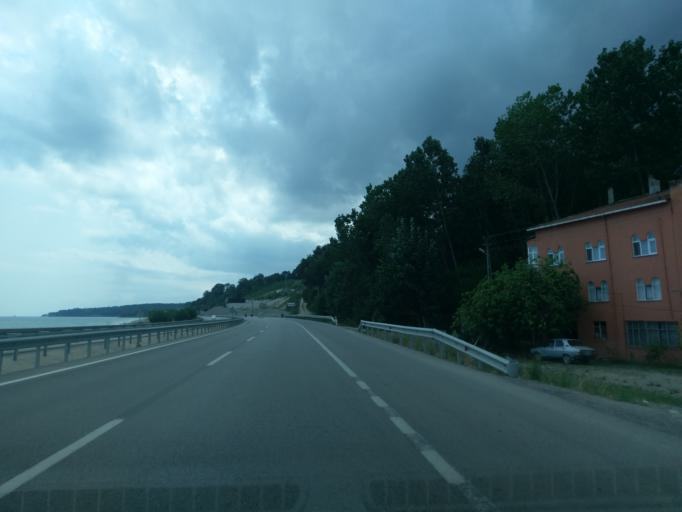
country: TR
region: Sinop
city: Gerze
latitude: 41.8318
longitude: 35.1589
